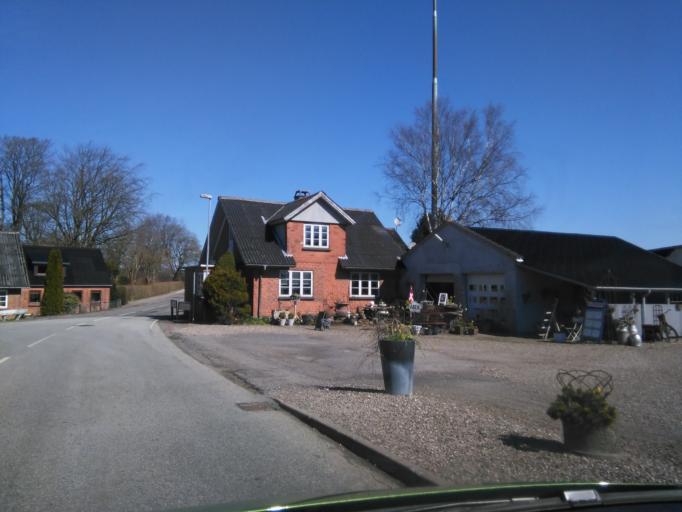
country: DK
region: Central Jutland
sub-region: Horsens Kommune
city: Braedstrup
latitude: 56.0214
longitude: 9.6423
